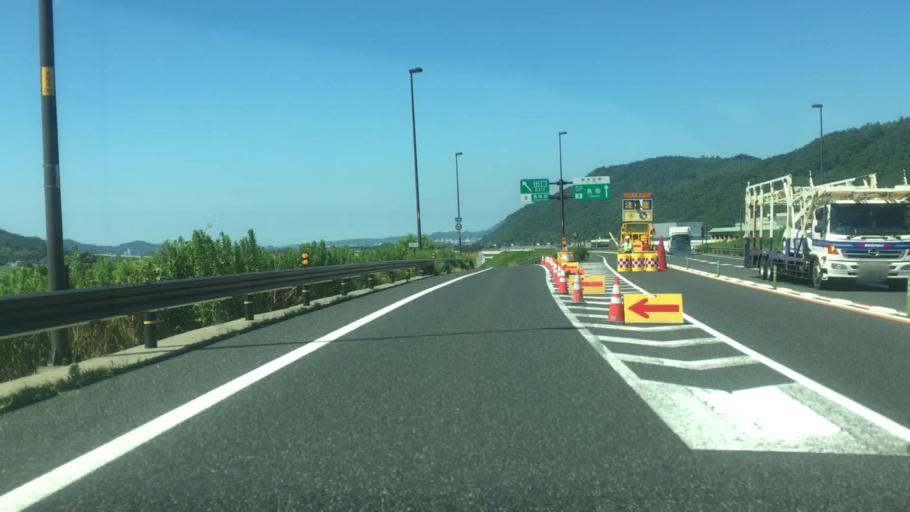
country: JP
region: Tottori
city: Tottori
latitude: 35.4211
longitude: 134.2061
